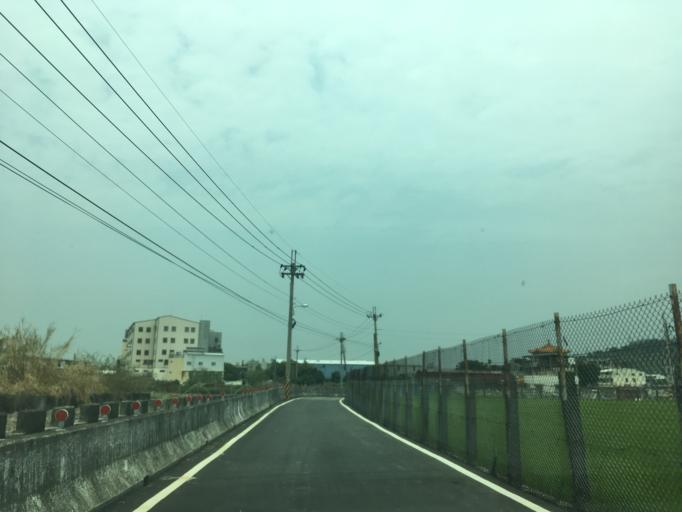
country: TW
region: Taiwan
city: Zhongxing New Village
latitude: 24.0350
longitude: 120.6892
